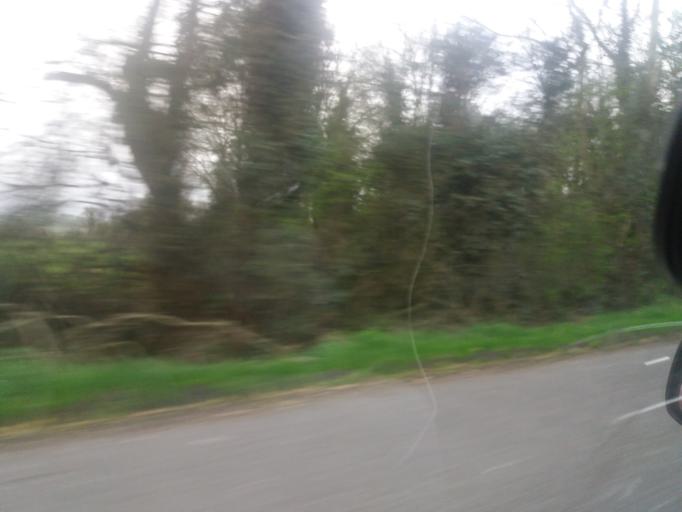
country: IE
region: Munster
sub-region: County Limerick
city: Newcastle West
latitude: 52.4808
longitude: -9.0115
